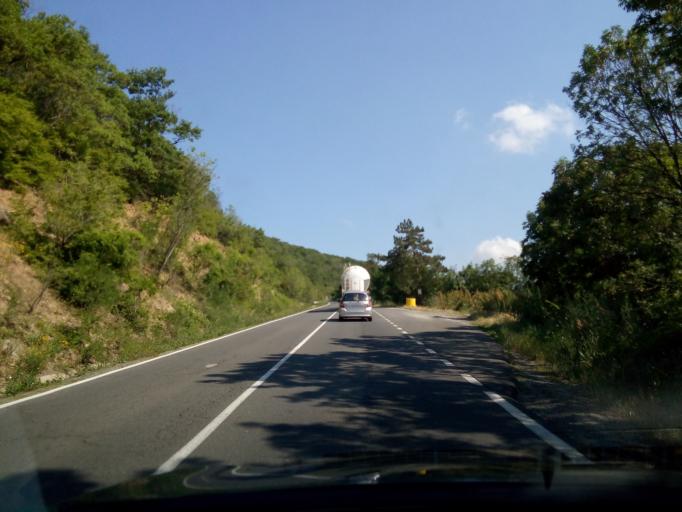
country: BG
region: Burgas
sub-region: Obshtina Nesebur
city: Sveti Vlas
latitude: 42.7308
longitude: 27.7397
